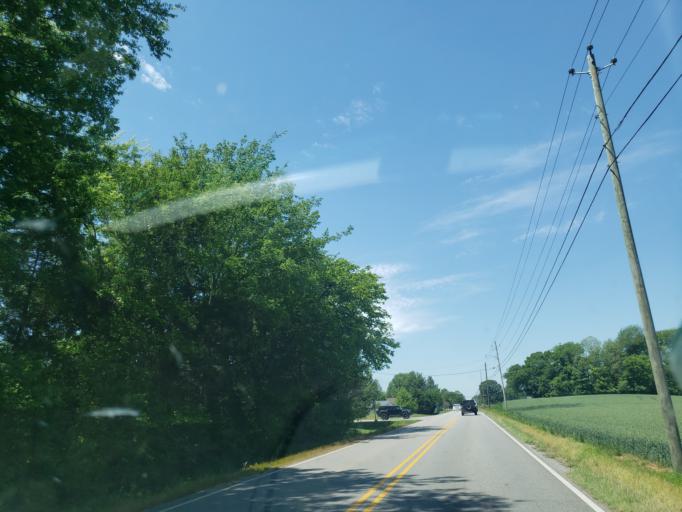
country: US
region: Alabama
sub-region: Madison County
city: Hazel Green
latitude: 34.9322
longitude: -86.5389
